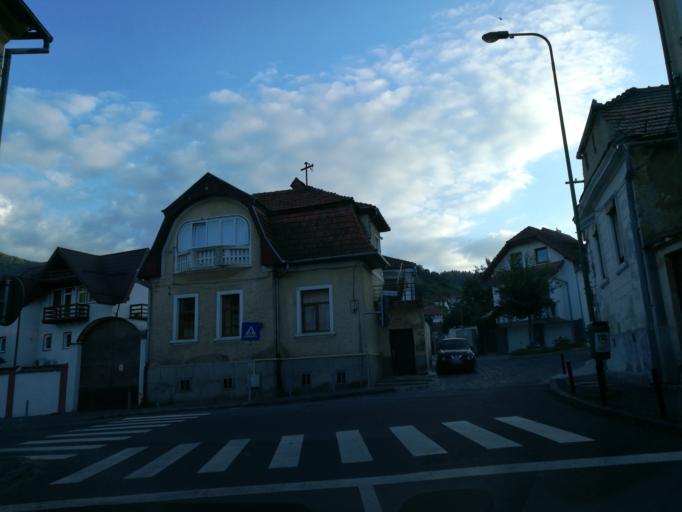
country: RO
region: Brasov
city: Brasov
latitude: 45.6367
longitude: 25.5791
